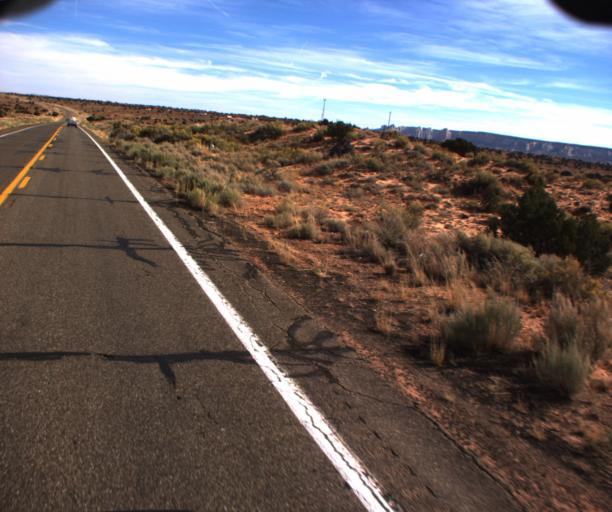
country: US
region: Arizona
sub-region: Coconino County
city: Kaibito
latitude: 36.5770
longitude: -111.1165
